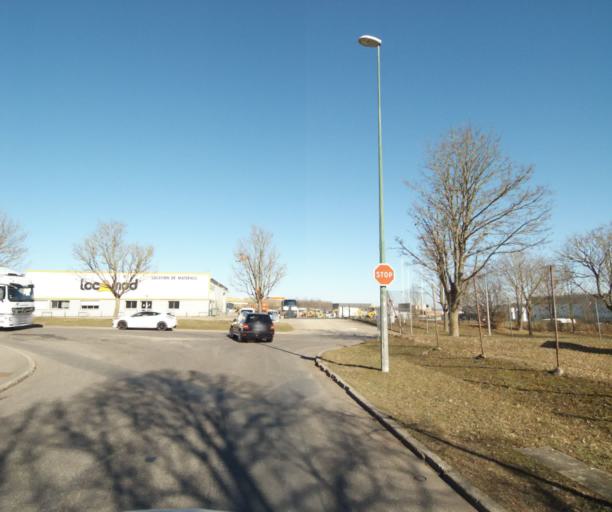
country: FR
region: Lorraine
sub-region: Departement de Meurthe-et-Moselle
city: Richardmenil
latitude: 48.6123
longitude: 6.1860
